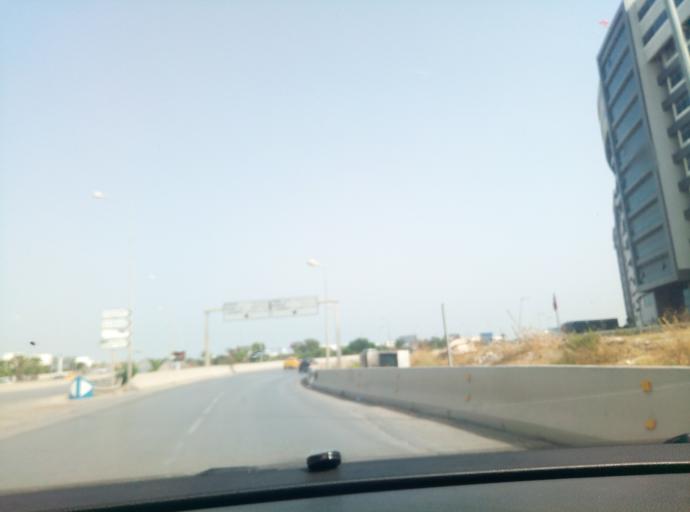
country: TN
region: Ariana
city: Ariana
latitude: 36.8506
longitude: 10.1993
